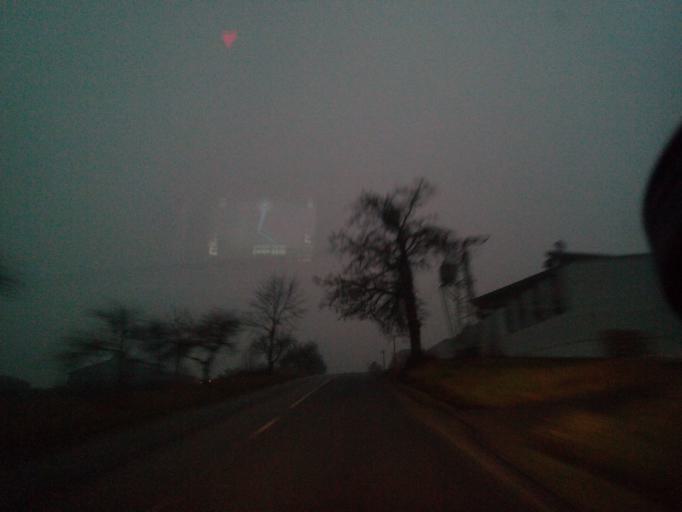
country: SK
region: Presovsky
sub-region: Okres Presov
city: Presov
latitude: 49.0175
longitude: 21.1874
